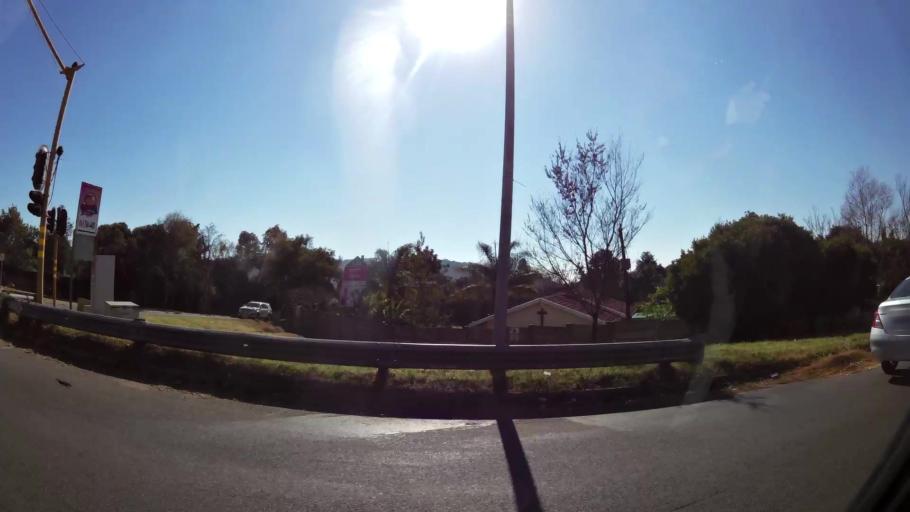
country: ZA
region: Gauteng
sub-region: City of Johannesburg Metropolitan Municipality
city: Roodepoort
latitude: -26.1236
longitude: 27.8669
